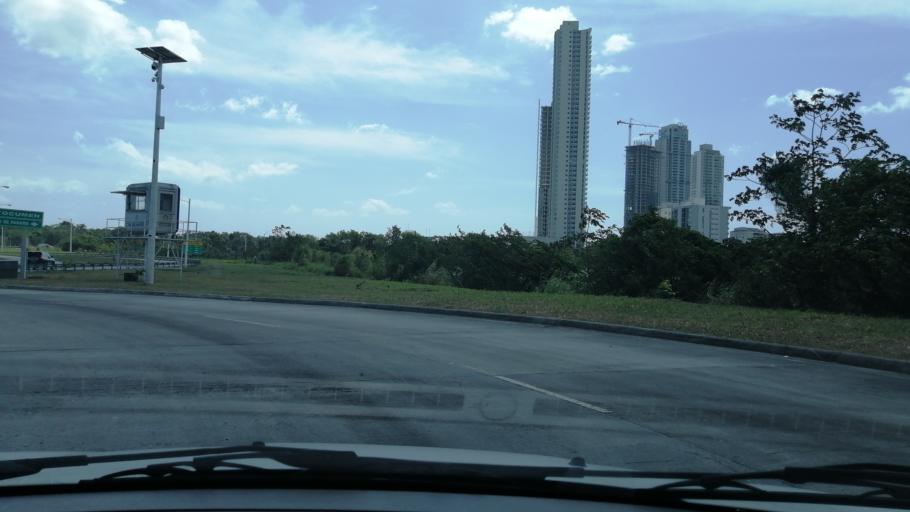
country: PA
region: Panama
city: San Miguelito
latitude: 9.0341
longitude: -79.4466
